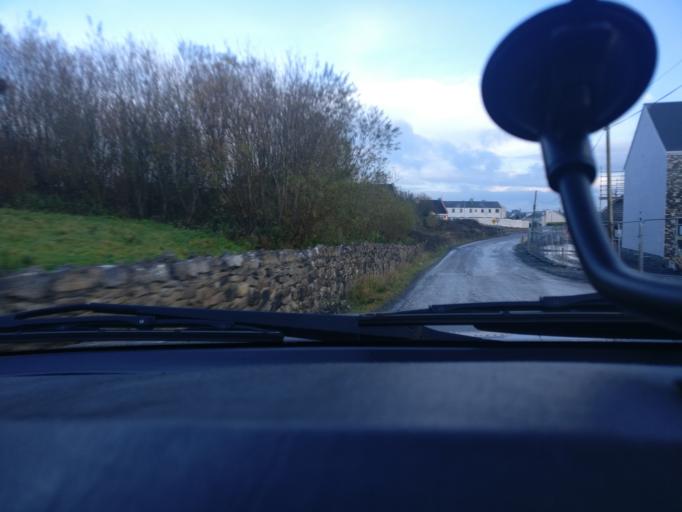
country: IE
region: Connaught
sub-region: County Galway
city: Loughrea
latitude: 53.1985
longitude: -8.5918
